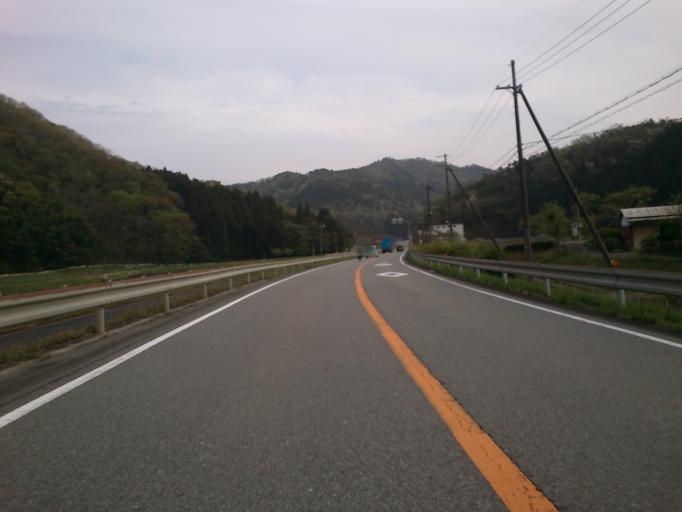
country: JP
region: Hyogo
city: Sasayama
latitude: 35.1245
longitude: 135.3363
